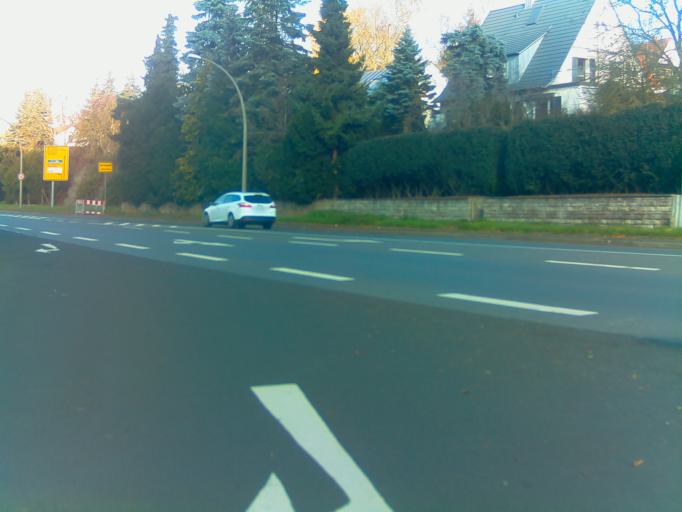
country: DE
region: Bavaria
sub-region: Regierungsbezirk Unterfranken
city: Bad Kissingen
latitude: 50.2158
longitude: 10.0723
